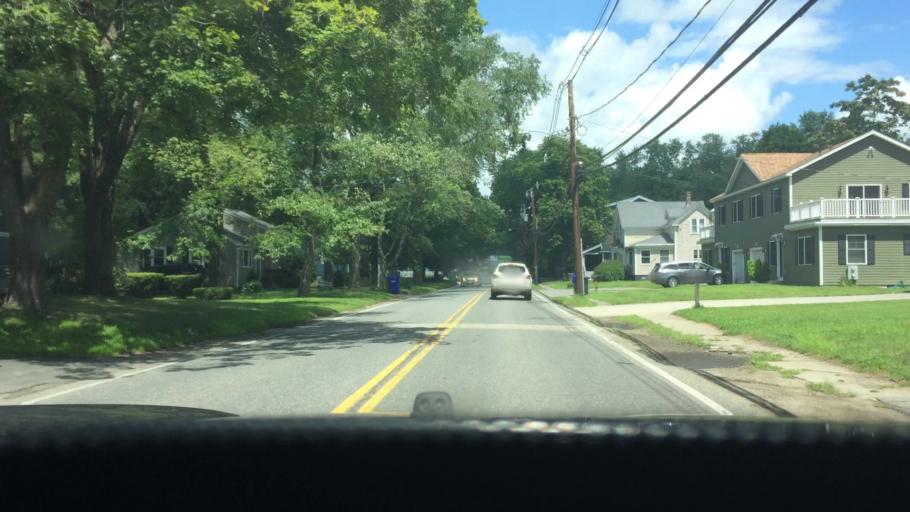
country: US
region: Massachusetts
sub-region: Middlesex County
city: Maynard
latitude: 42.4401
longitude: -71.4524
